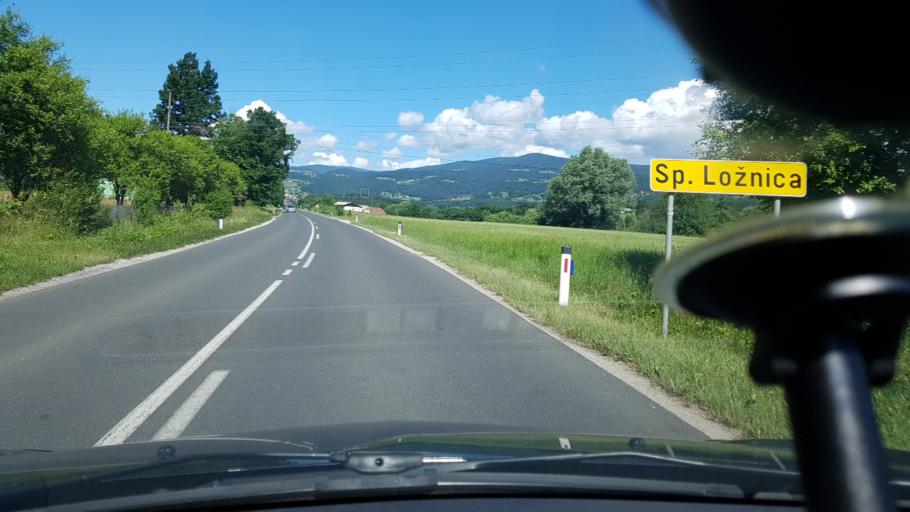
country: SI
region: Slovenska Bistrica
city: Slovenska Bistrica
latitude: 46.3767
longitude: 15.5442
